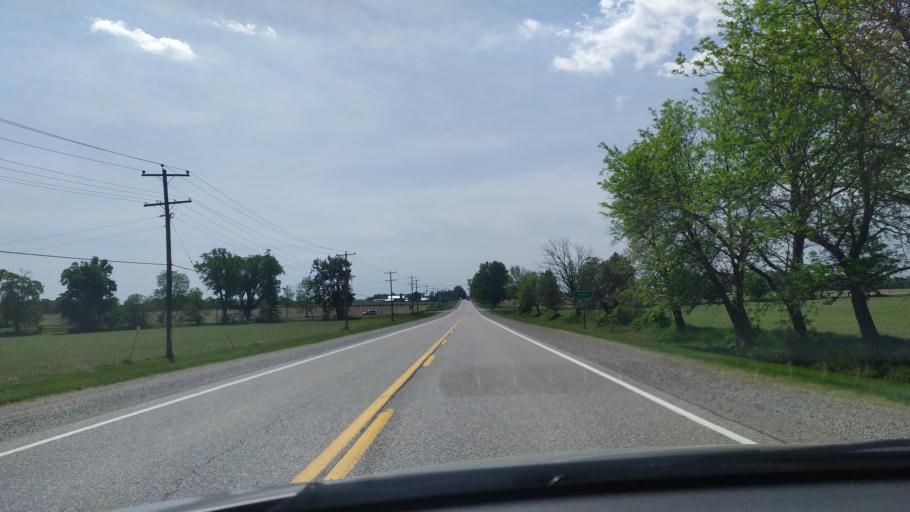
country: CA
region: Ontario
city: Dorchester
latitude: 43.0886
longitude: -81.0044
